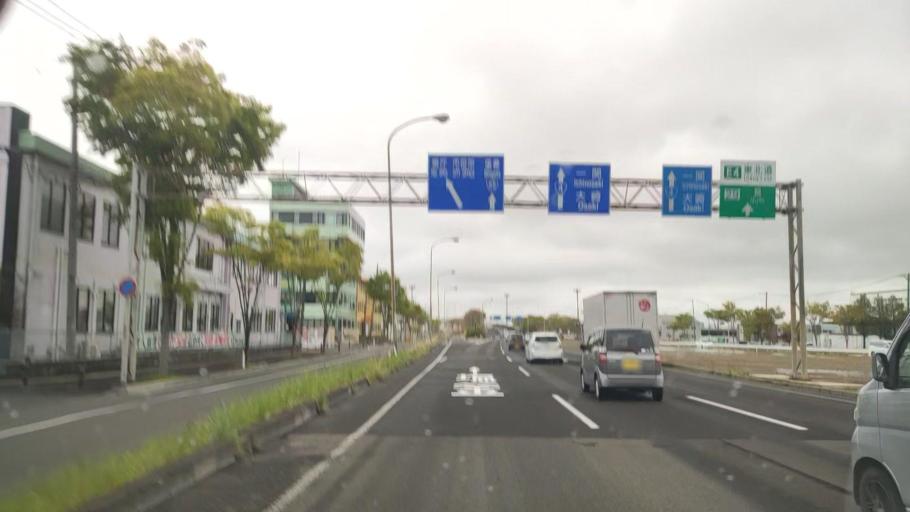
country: JP
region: Miyagi
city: Sendai-shi
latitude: 38.2632
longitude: 140.9379
